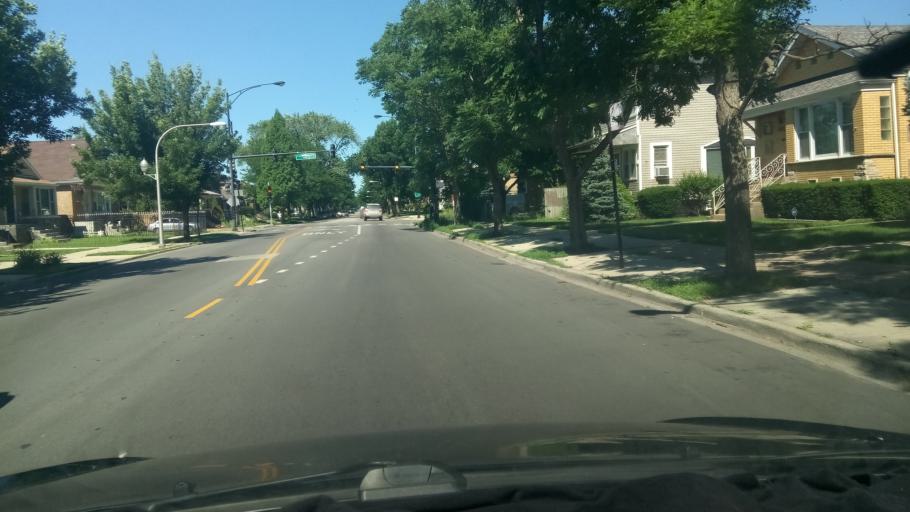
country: US
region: Illinois
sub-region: Cook County
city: Hometown
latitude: 41.7716
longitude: -87.7139
